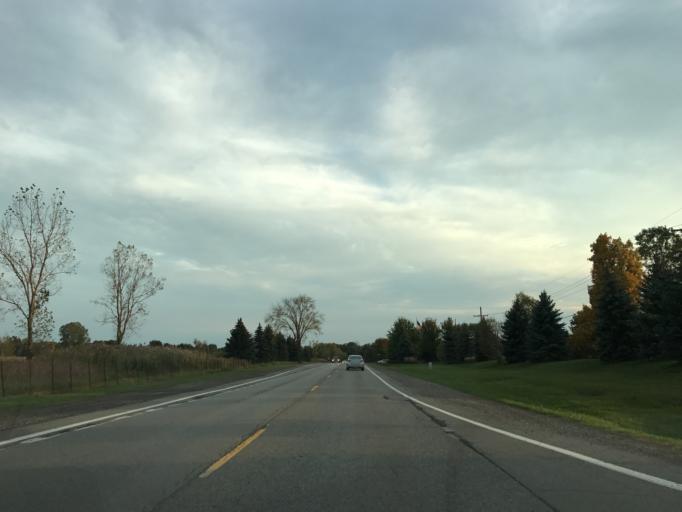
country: US
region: Michigan
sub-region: Oakland County
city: South Lyon
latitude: 42.4964
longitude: -83.6148
